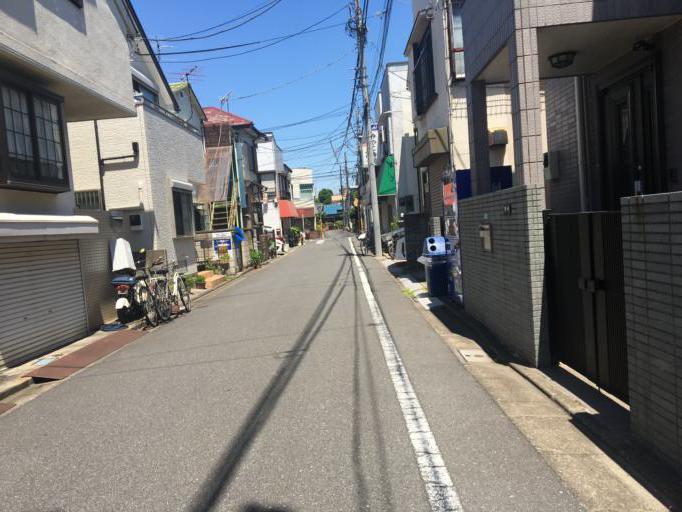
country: JP
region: Saitama
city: Wako
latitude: 35.7643
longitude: 139.6497
